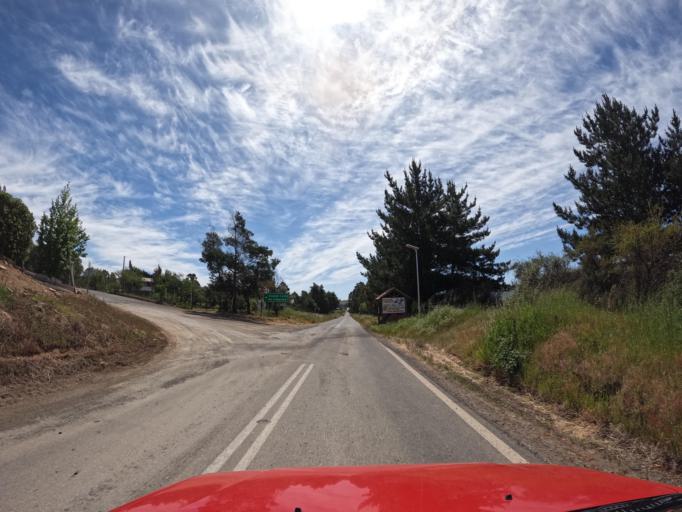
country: CL
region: Maule
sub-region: Provincia de Talca
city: Talca
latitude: -35.0392
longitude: -71.7548
